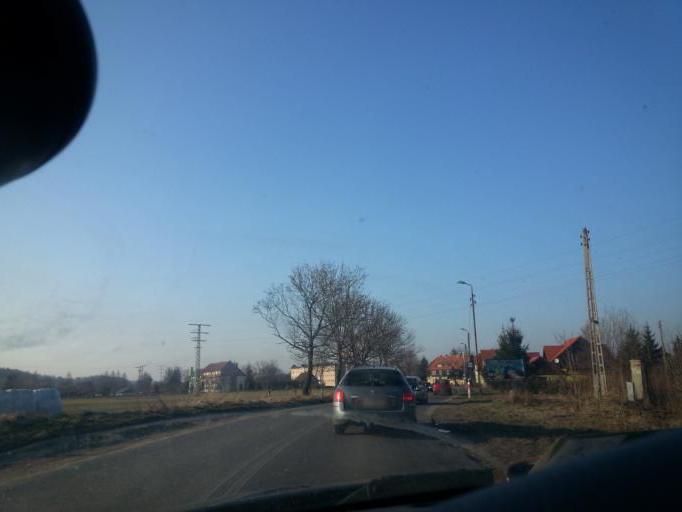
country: PL
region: Lower Silesian Voivodeship
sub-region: Powiat jeleniogorski
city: Myslakowice
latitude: 50.8450
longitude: 15.7863
